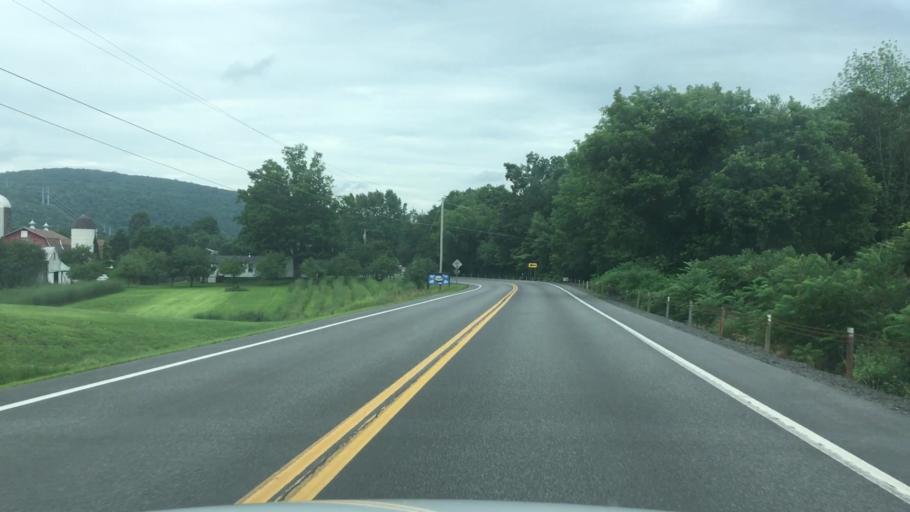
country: US
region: New York
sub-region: Otsego County
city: Otego
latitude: 42.4172
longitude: -75.1449
